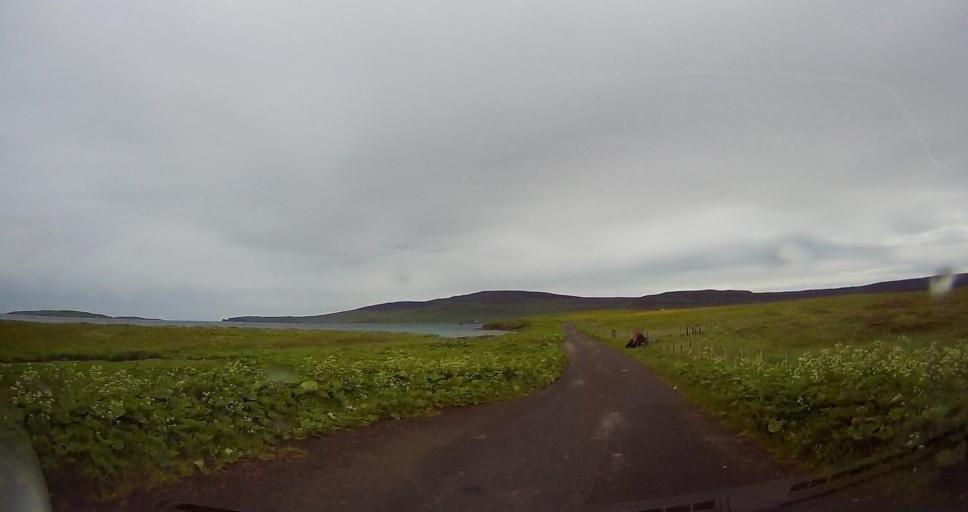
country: GB
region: Scotland
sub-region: Orkney Islands
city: Orkney
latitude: 59.1183
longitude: -3.0864
